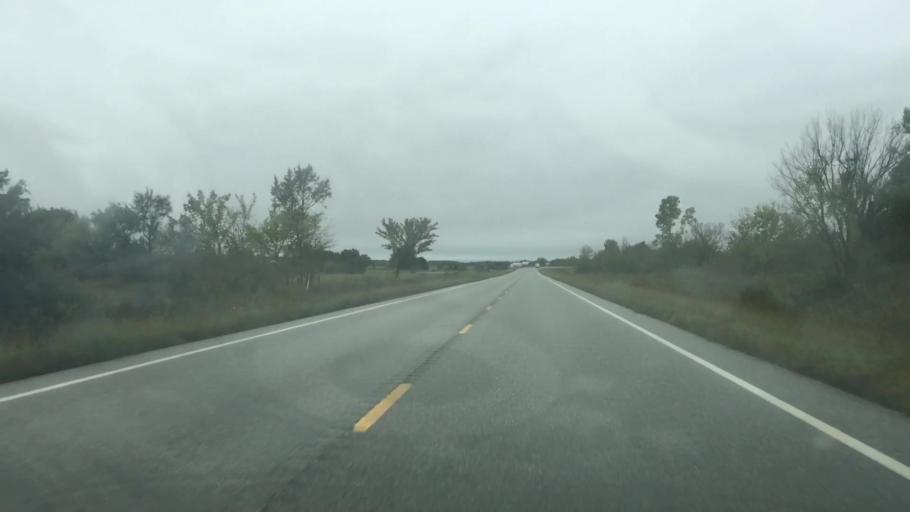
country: US
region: Kansas
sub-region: Anderson County
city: Garnett
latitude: 38.2873
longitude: -95.2077
